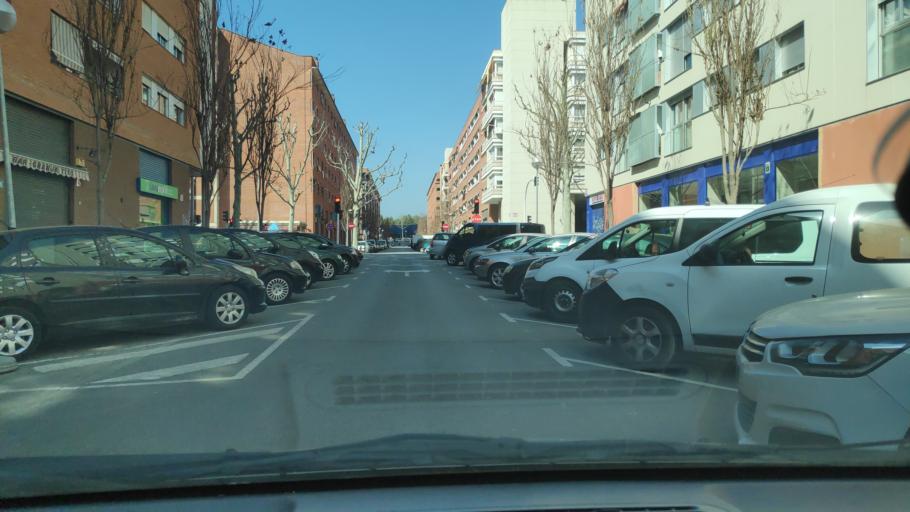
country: ES
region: Catalonia
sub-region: Provincia de Barcelona
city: Mollet del Valles
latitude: 41.5459
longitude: 2.2071
